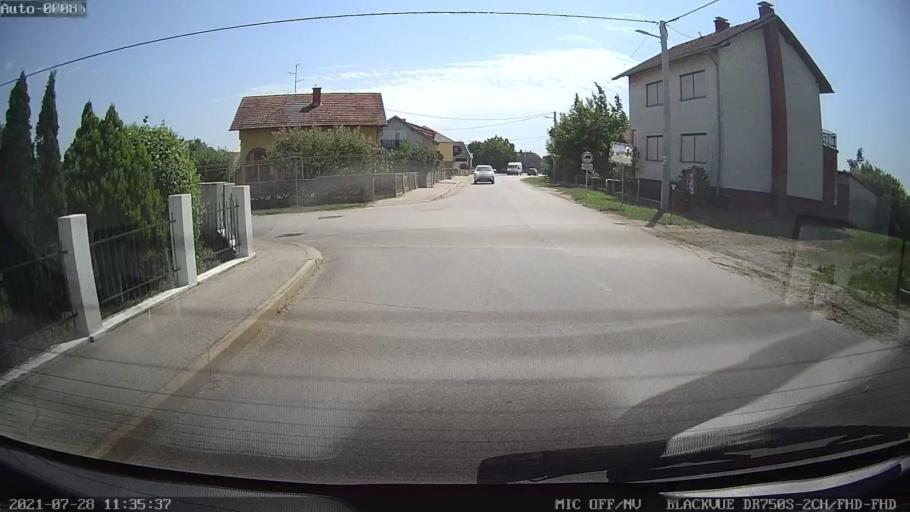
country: HR
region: Varazdinska
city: Varazdin
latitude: 46.2970
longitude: 16.3681
